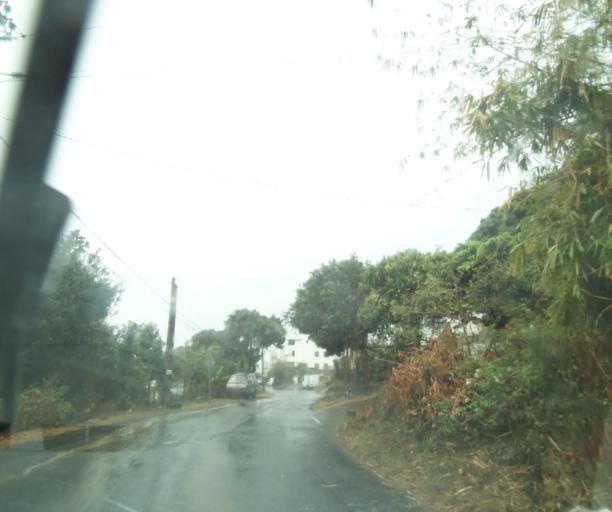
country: RE
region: Reunion
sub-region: Reunion
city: Saint-Paul
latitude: -20.9914
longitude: 55.3268
